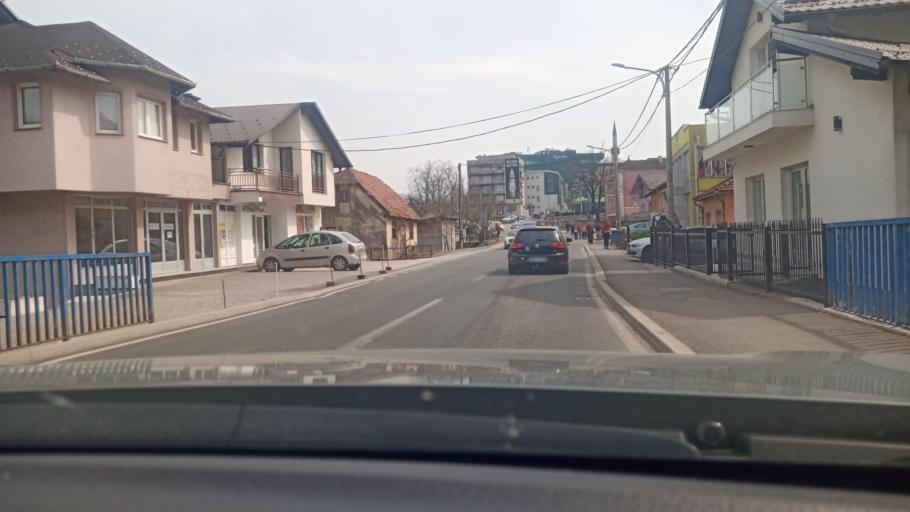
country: BA
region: Federation of Bosnia and Herzegovina
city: Bihac
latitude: 44.8176
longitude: 15.8667
